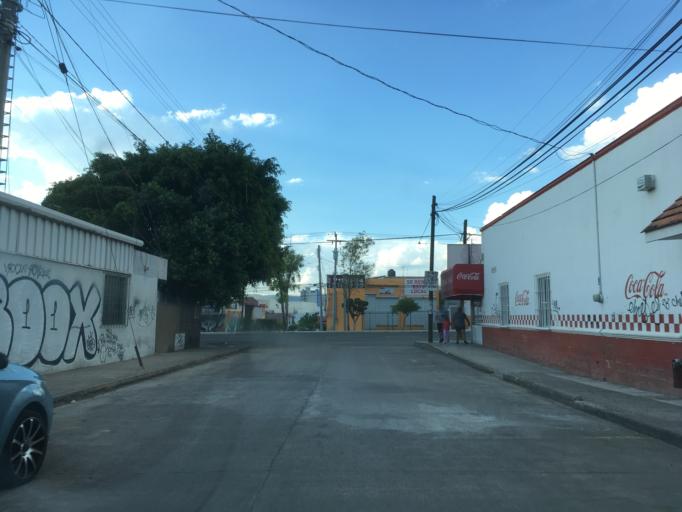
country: MX
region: Guanajuato
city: Leon
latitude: 21.0967
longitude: -101.6377
